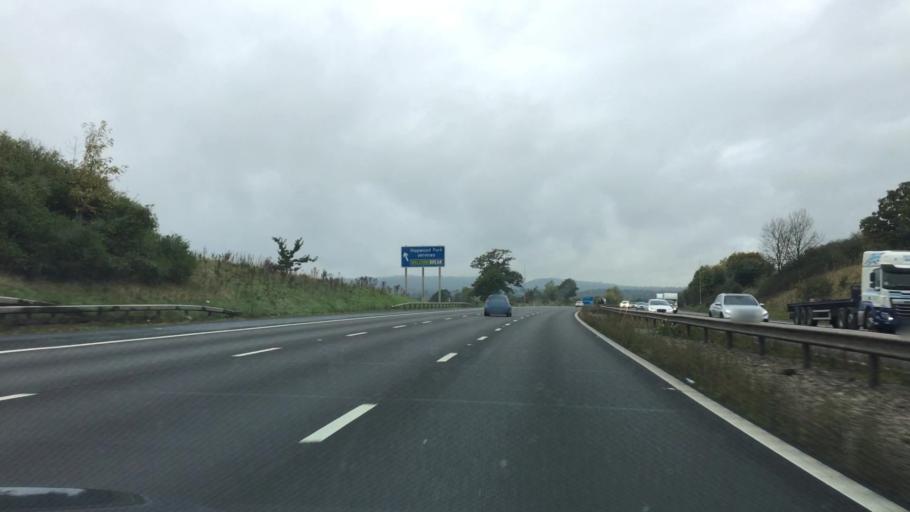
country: GB
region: England
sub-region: Worcestershire
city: Alvechurch
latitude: 52.3559
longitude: -1.9248
